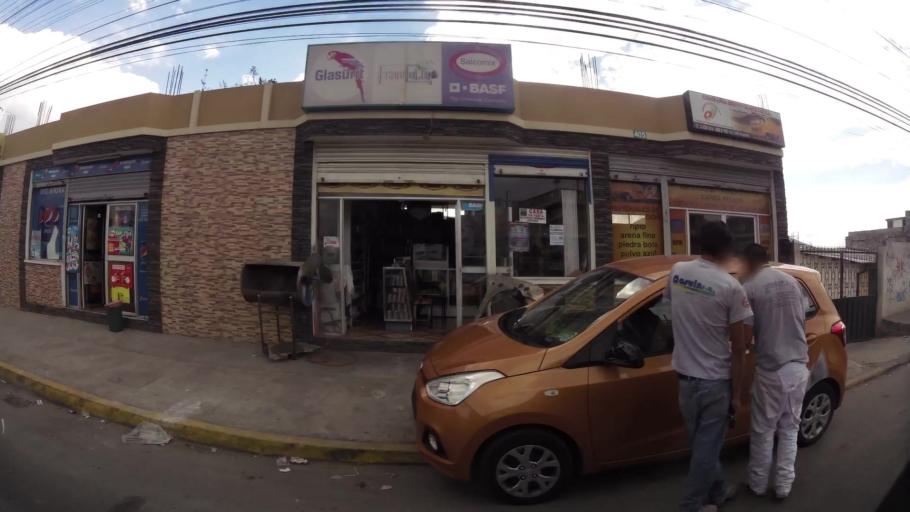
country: EC
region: Pichincha
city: Quito
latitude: -0.0974
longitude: -78.4446
